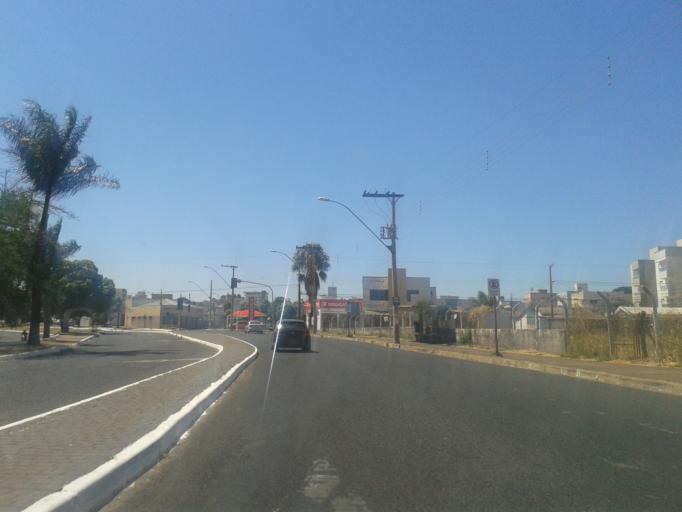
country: BR
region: Minas Gerais
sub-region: Uberlandia
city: Uberlandia
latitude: -18.8993
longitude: -48.2698
